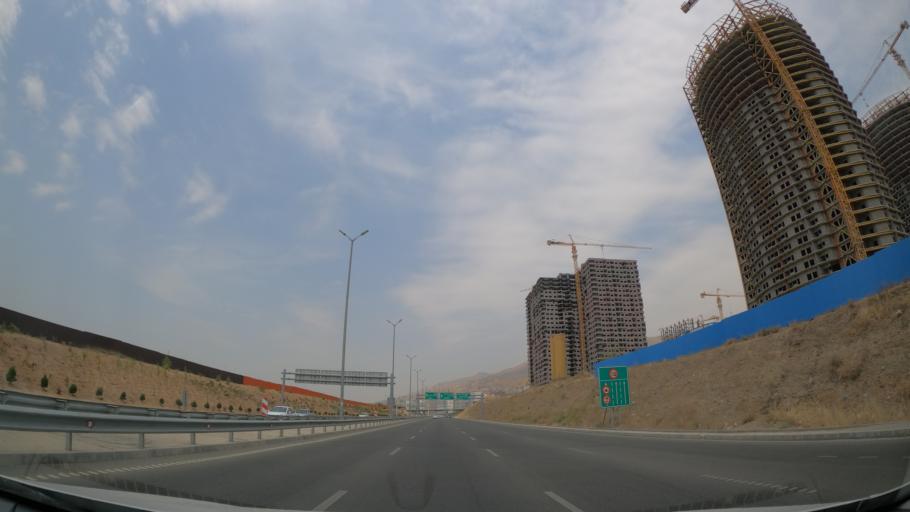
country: IR
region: Tehran
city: Shahr-e Qods
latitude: 35.7477
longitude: 51.1795
